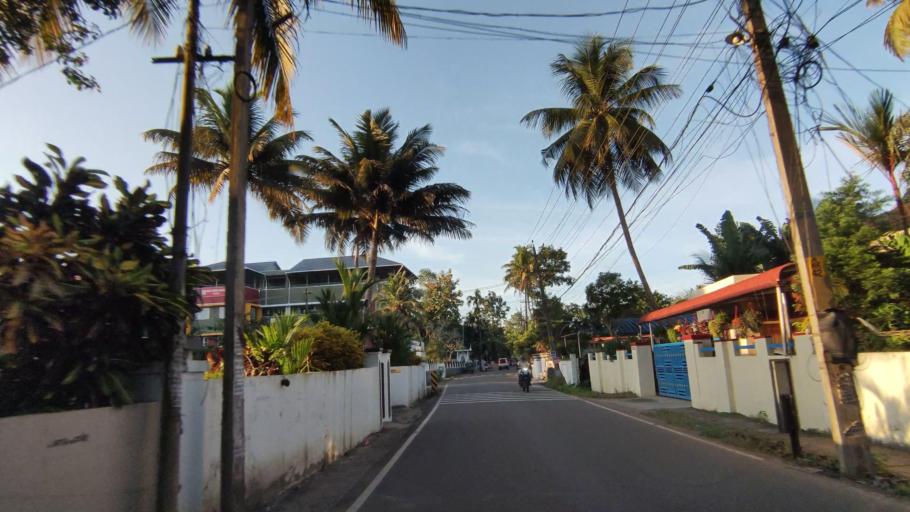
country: IN
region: Kerala
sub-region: Kottayam
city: Kottayam
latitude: 9.6168
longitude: 76.4939
